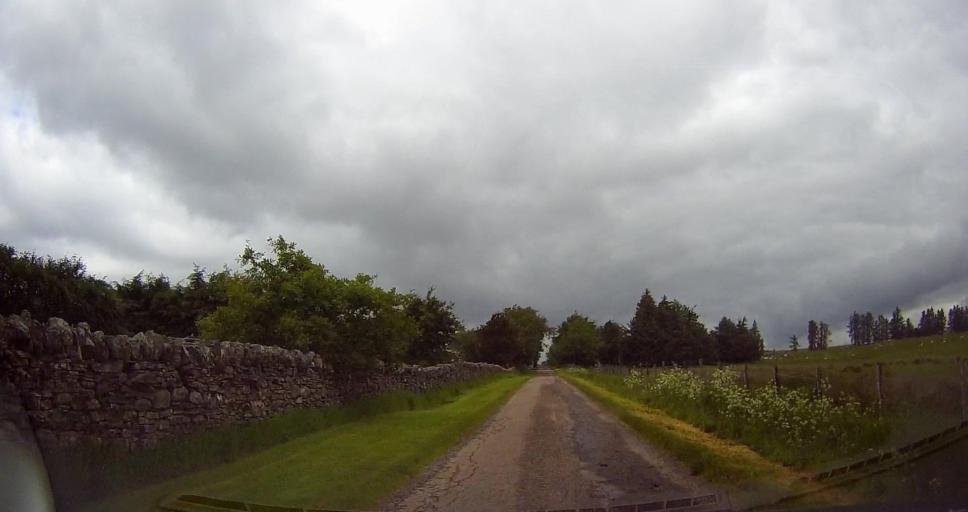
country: GB
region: Scotland
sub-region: Highland
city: Alness
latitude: 58.0746
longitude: -4.4397
